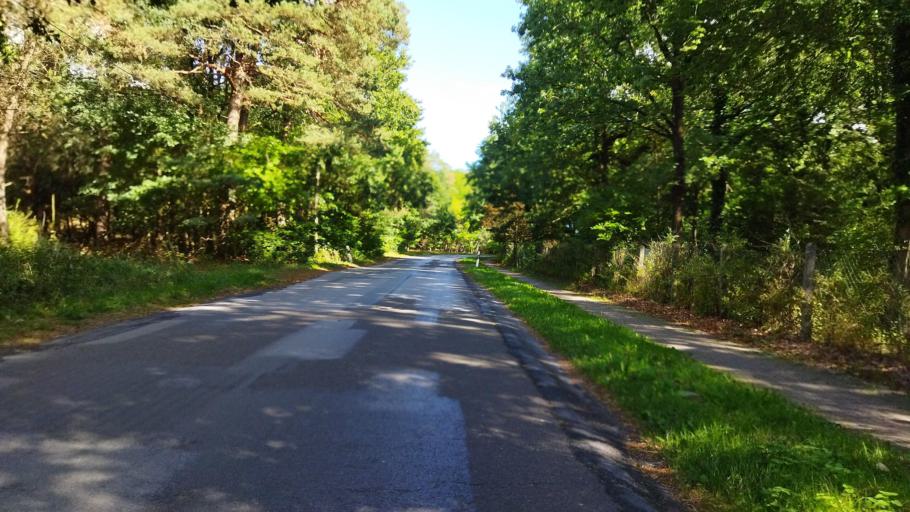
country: DE
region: Lower Saxony
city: Lingen
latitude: 52.4546
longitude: 7.3506
